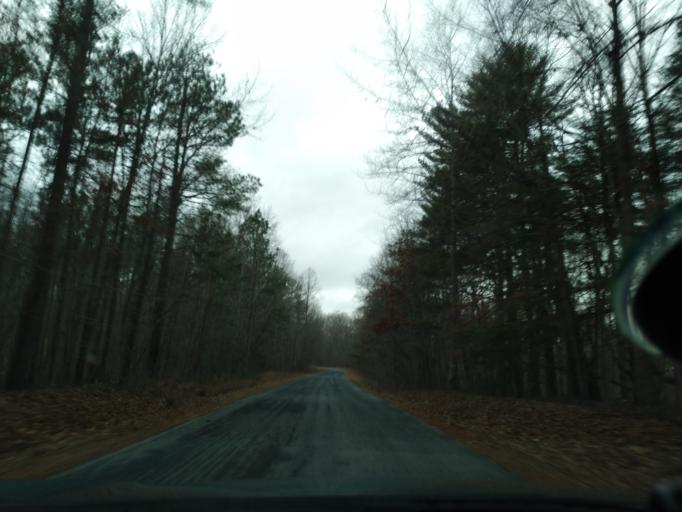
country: US
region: Virginia
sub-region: Appomattox County
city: Appomattox
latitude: 37.4206
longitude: -78.6686
